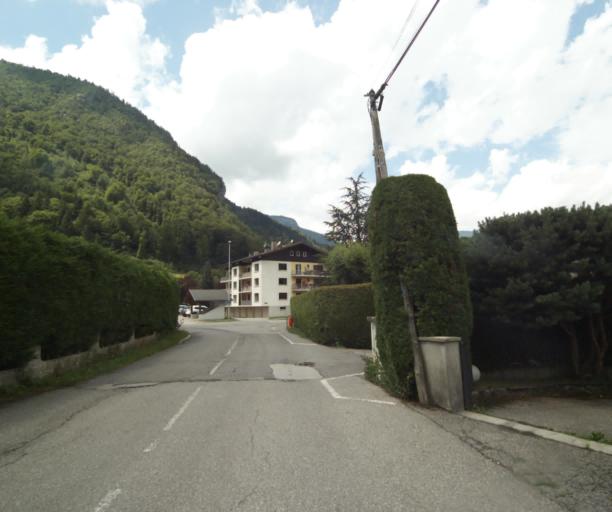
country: FR
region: Rhone-Alpes
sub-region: Departement de la Haute-Savoie
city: Thones
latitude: 45.8774
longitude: 6.3223
